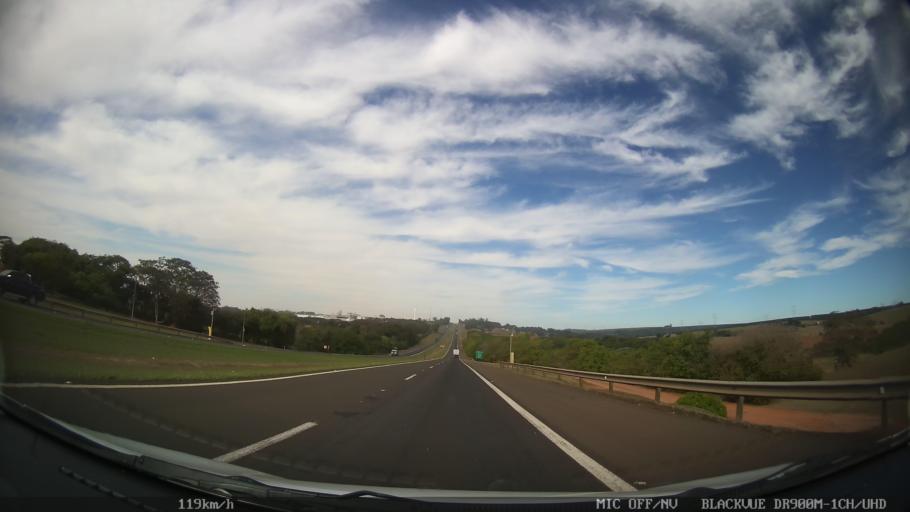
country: BR
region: Sao Paulo
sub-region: Matao
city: Matao
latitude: -21.5846
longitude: -48.4485
